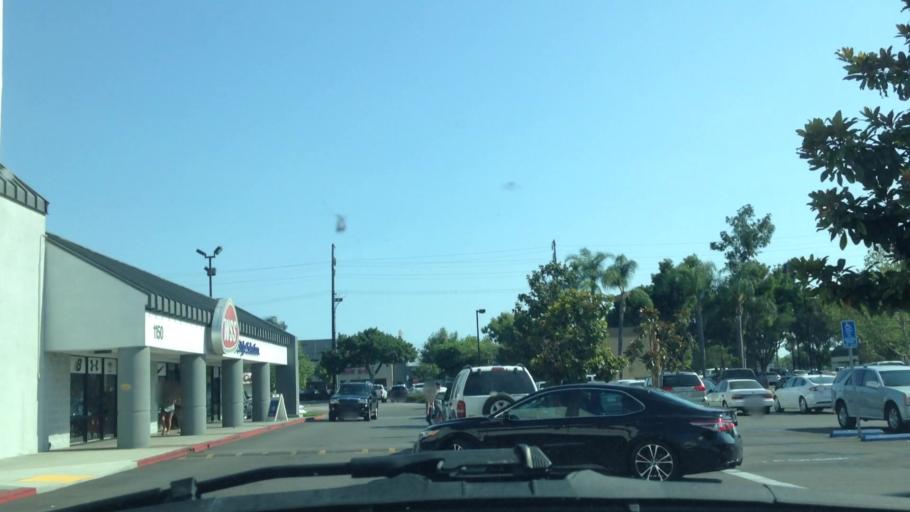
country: US
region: California
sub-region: Orange County
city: Fullerton
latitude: 33.8607
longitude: -117.9230
